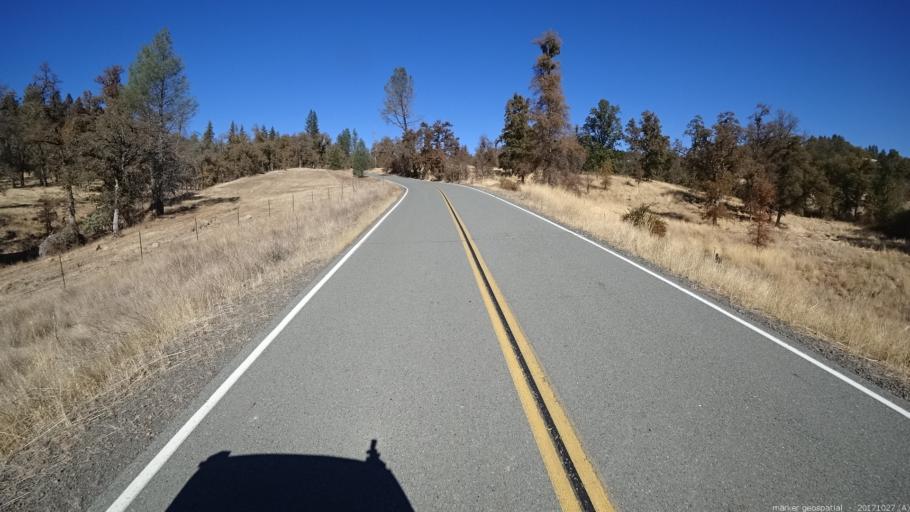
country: US
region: California
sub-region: Shasta County
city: Bella Vista
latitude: 40.7440
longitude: -121.9933
